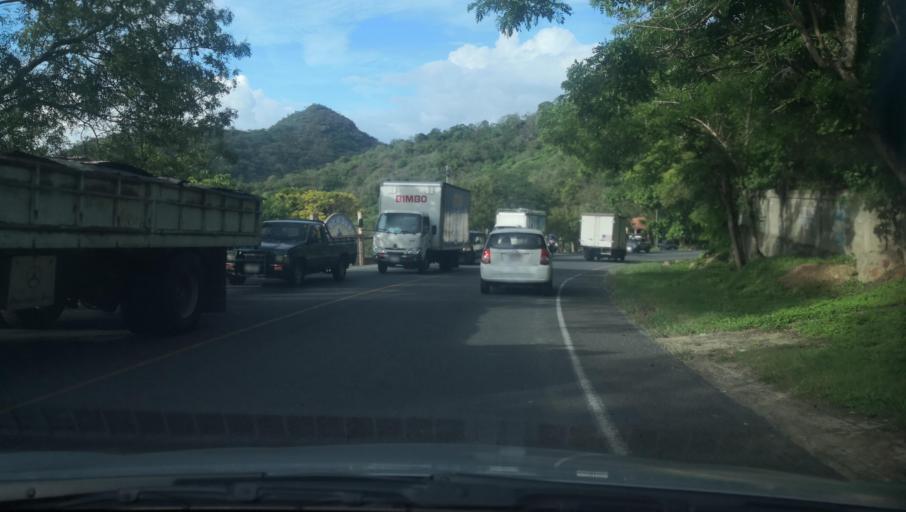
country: NI
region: Madriz
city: Totogalpa
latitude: 13.5880
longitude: -86.4733
